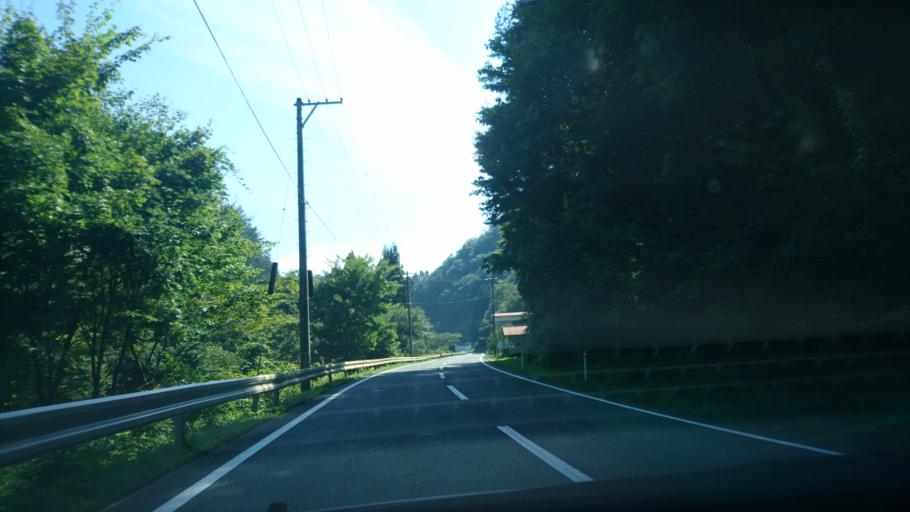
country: JP
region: Iwate
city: Ofunato
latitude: 39.0192
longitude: 141.4981
